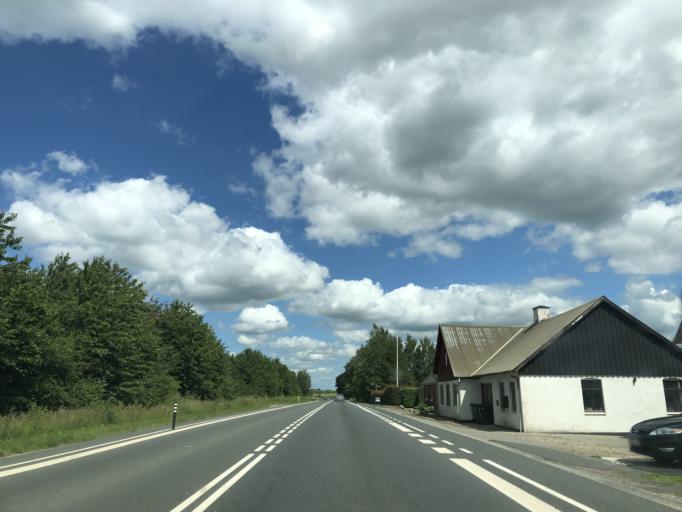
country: DK
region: Central Jutland
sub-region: Silkeborg Kommune
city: Svejbaek
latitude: 56.2150
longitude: 9.6161
